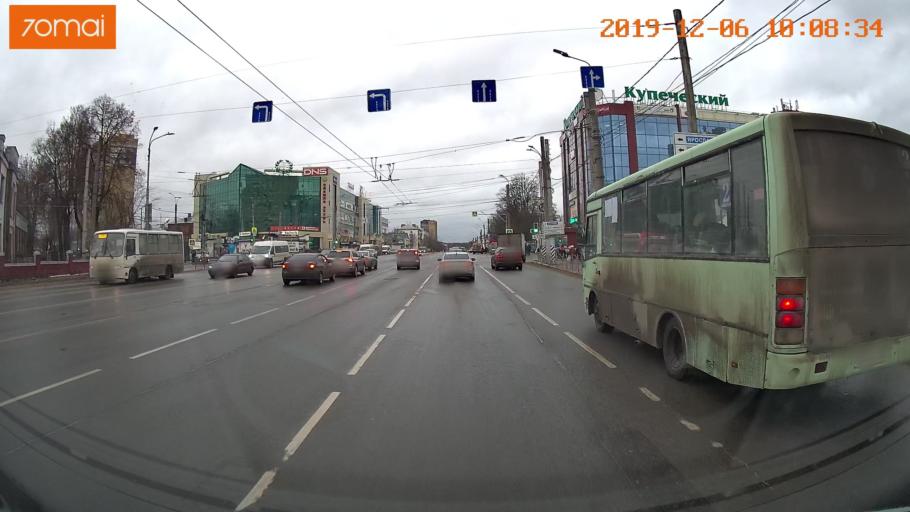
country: RU
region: Ivanovo
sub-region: Gorod Ivanovo
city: Ivanovo
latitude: 57.0164
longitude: 40.9698
